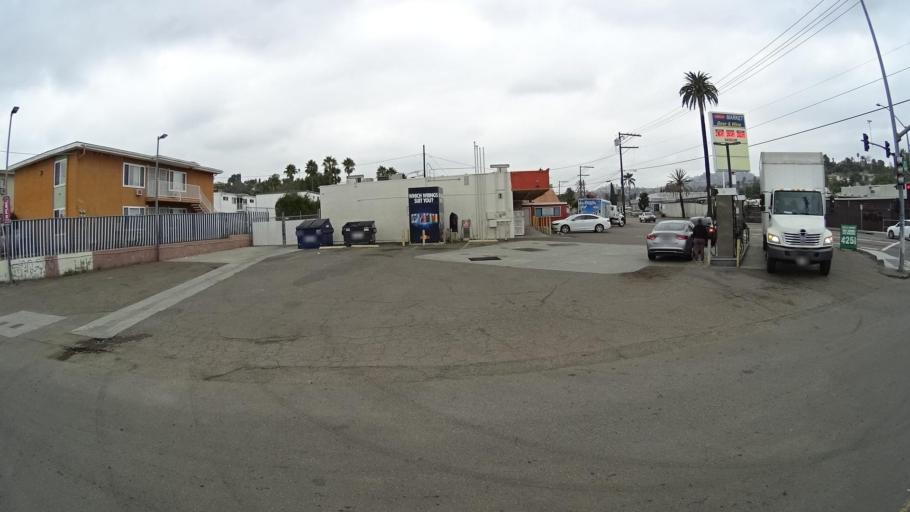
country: US
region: California
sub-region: San Diego County
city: Spring Valley
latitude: 32.7445
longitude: -117.0038
